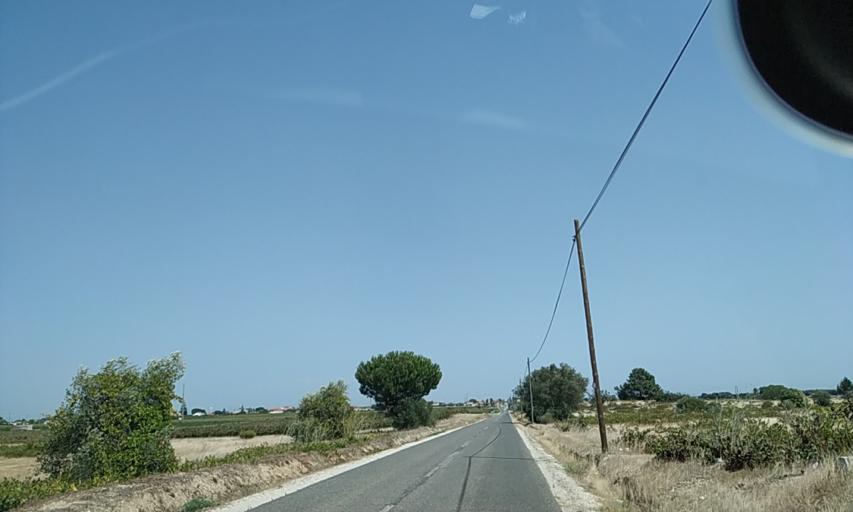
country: PT
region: Setubal
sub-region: Palmela
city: Palmela
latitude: 38.6046
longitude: -8.8294
